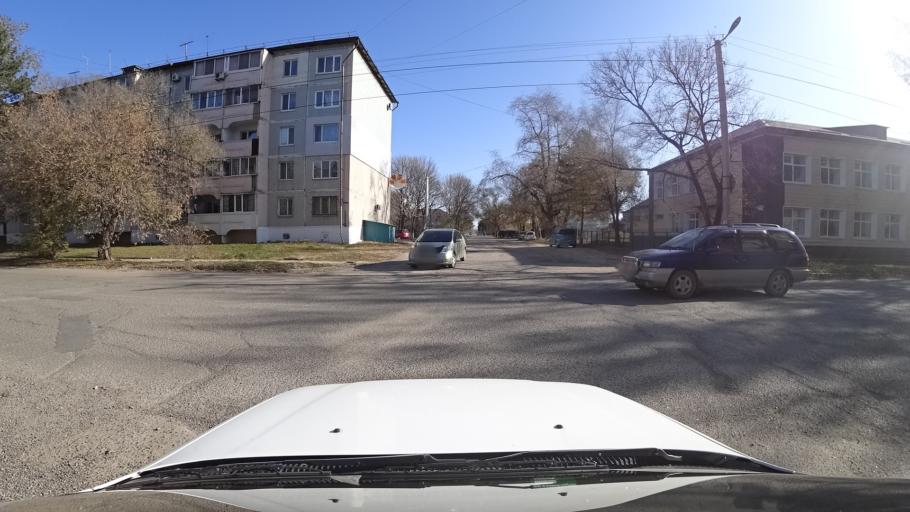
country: RU
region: Primorskiy
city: Dal'nerechensk
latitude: 45.9349
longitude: 133.7339
